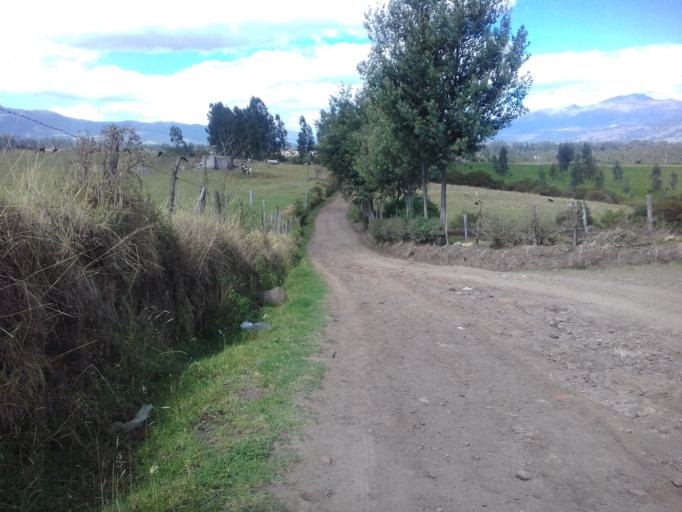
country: EC
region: Pichincha
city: Sangolqui
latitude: -0.3509
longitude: -78.4045
